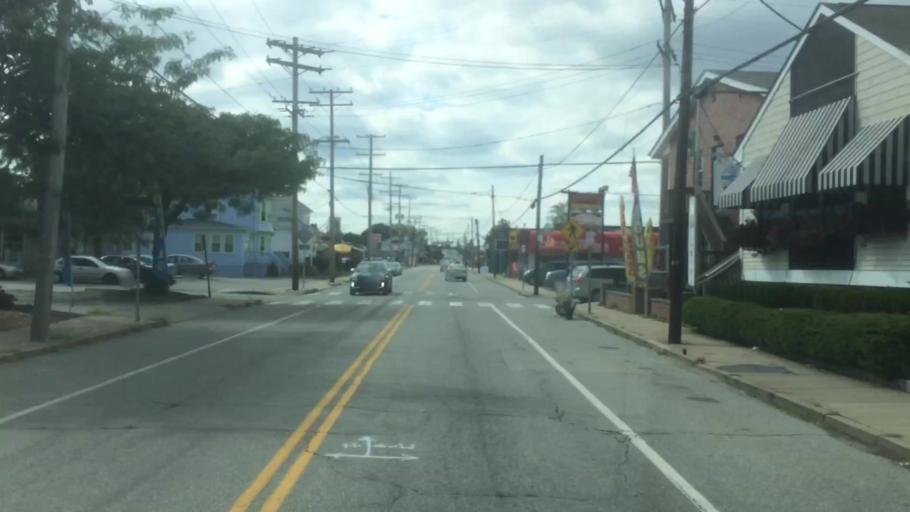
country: US
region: Rhode Island
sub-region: Providence County
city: Cranston
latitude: 41.7819
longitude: -71.4425
